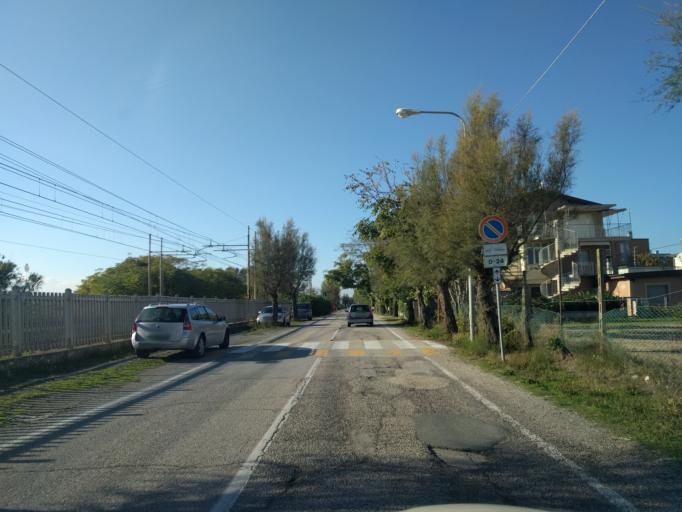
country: IT
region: The Marches
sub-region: Provincia di Pesaro e Urbino
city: Marotta
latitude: 43.7960
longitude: 13.0989
